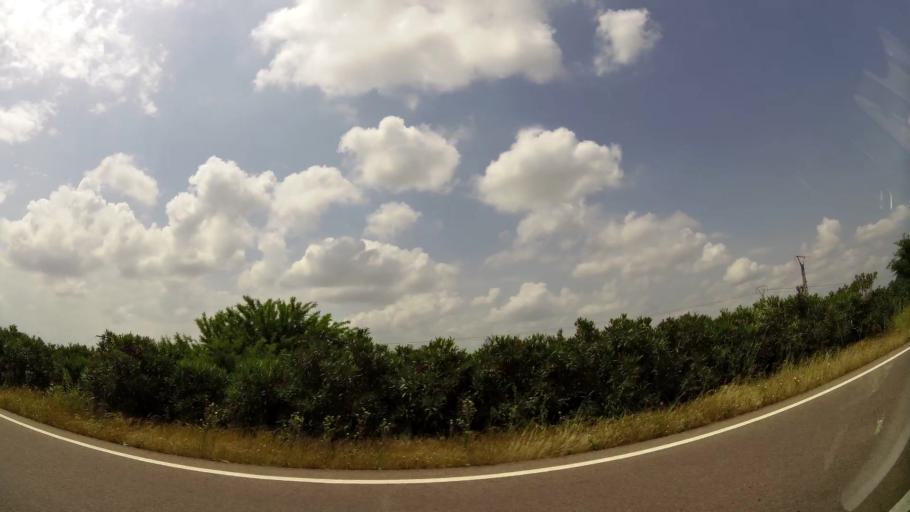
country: MA
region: Rabat-Sale-Zemmour-Zaer
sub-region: Khemisset
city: Tiflet
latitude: 33.9778
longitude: -6.5166
